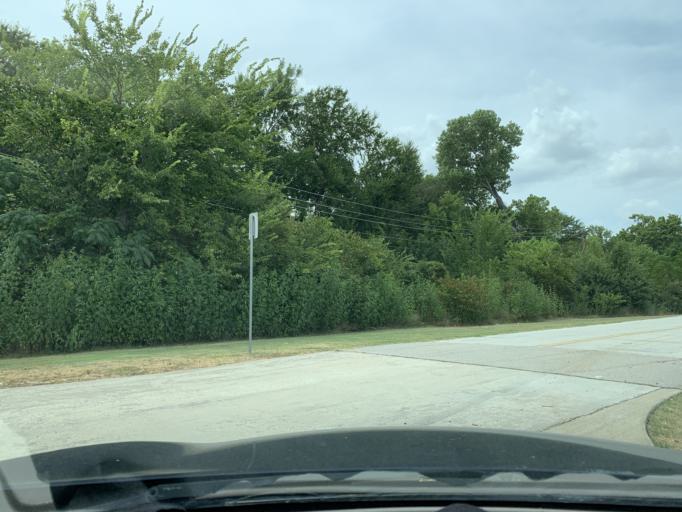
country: US
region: Texas
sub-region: Dallas County
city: Grand Prairie
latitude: 32.6664
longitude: -97.0303
